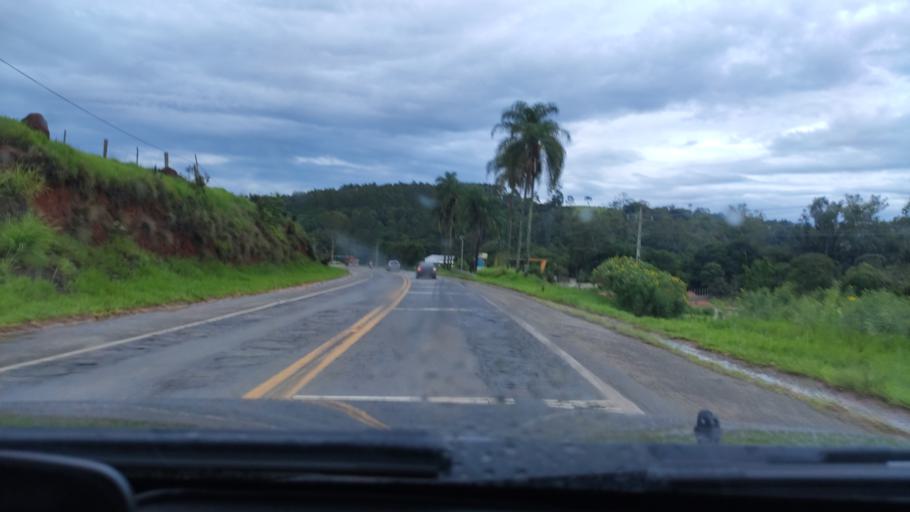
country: BR
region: Sao Paulo
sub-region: Braganca Paulista
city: Braganca Paulista
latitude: -22.7934
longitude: -46.5551
